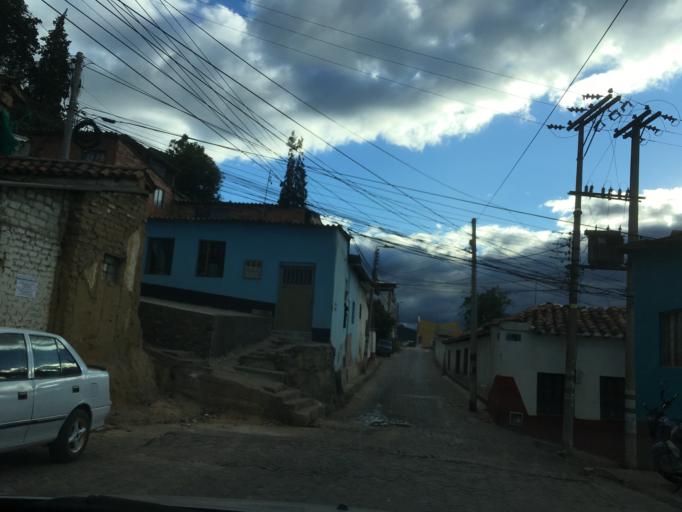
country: CO
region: Boyaca
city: Sogamoso
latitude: 5.7148
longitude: -72.9244
